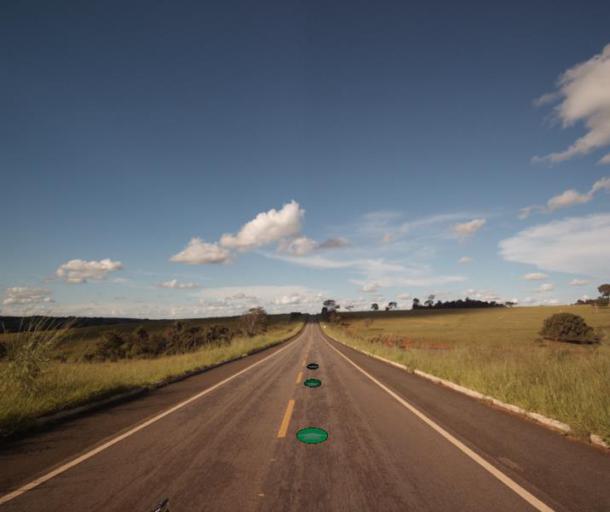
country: BR
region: Goias
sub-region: Itaberai
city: Itaberai
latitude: -15.9704
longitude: -49.6720
